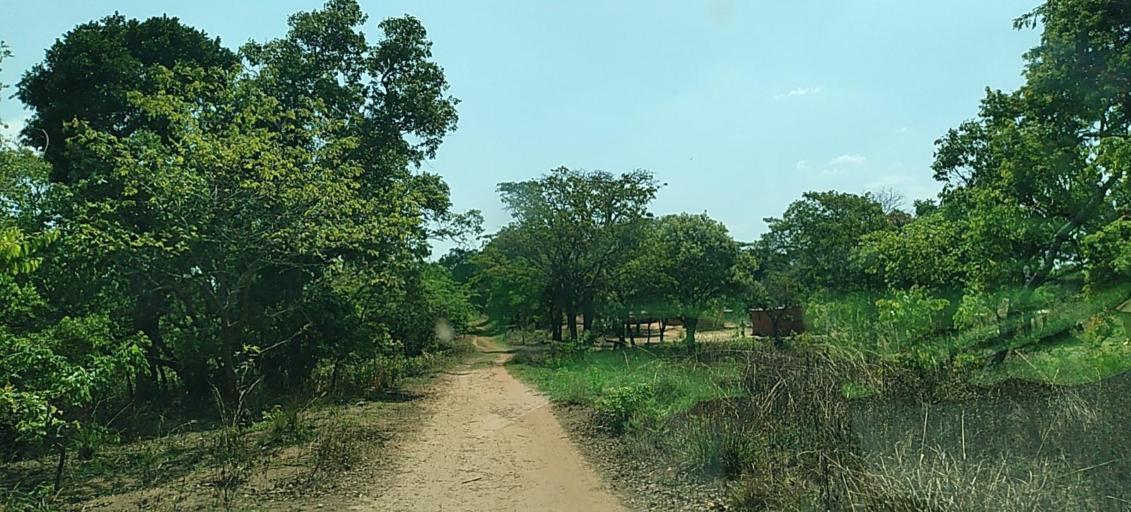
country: CD
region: Katanga
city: Kolwezi
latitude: -11.2821
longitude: 25.1453
